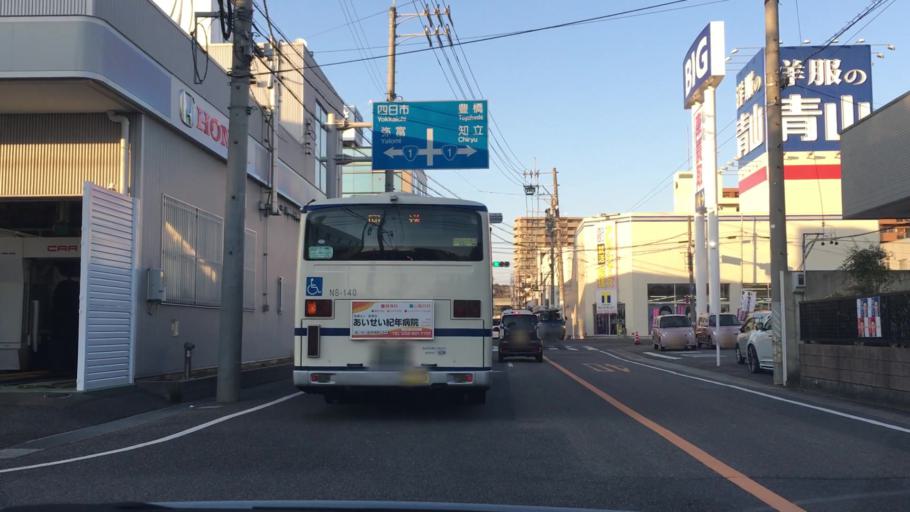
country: JP
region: Aichi
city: Obu
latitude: 35.0772
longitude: 136.9463
